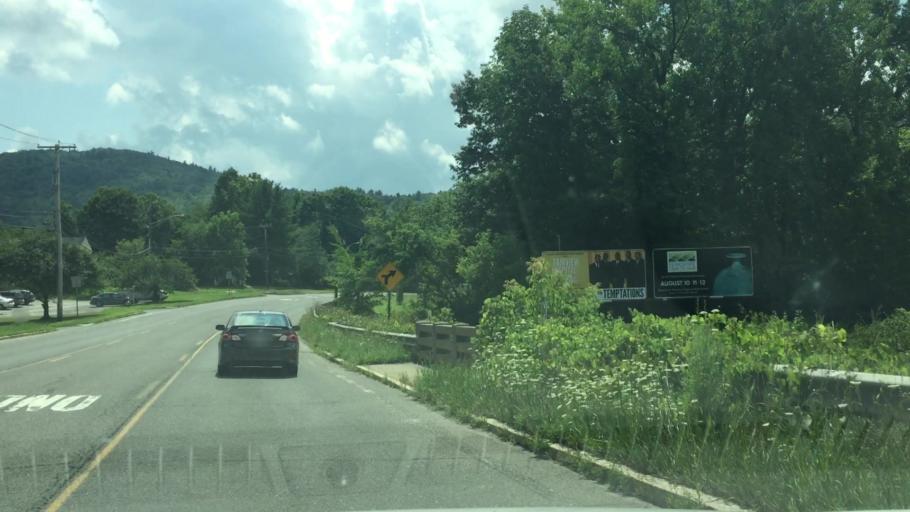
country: US
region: Massachusetts
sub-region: Berkshire County
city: Great Barrington
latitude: 42.2037
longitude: -73.3469
